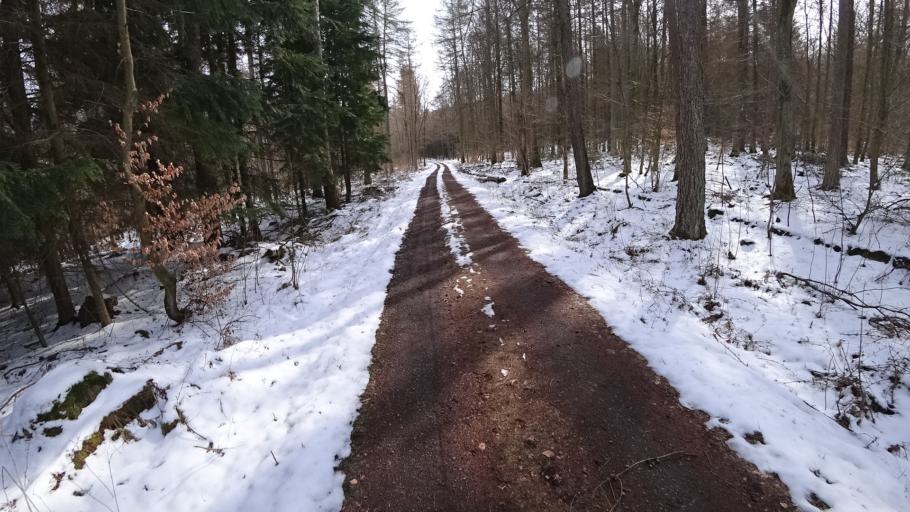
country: DE
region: Rheinland-Pfalz
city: Nauroth
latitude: 50.6836
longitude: 7.8591
